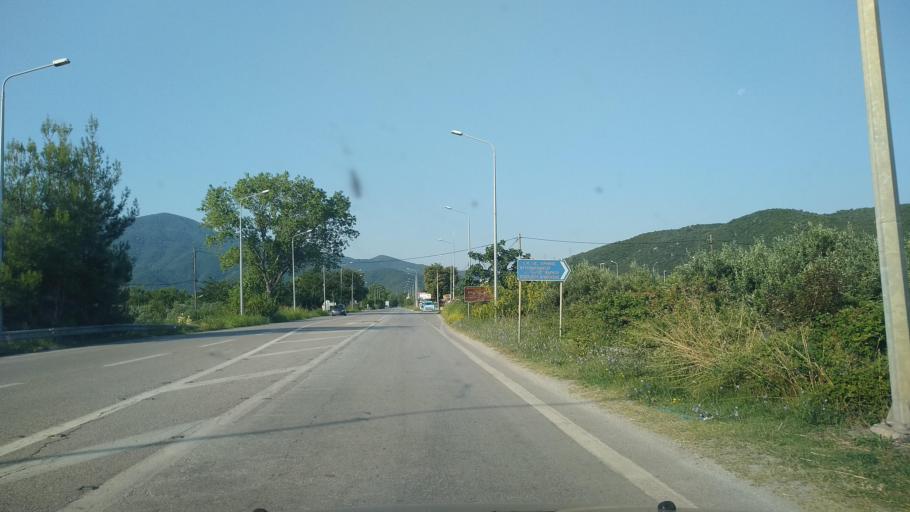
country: GR
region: Central Macedonia
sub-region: Nomos Thessalonikis
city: Nea Vrasna
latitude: 40.6913
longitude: 23.6830
